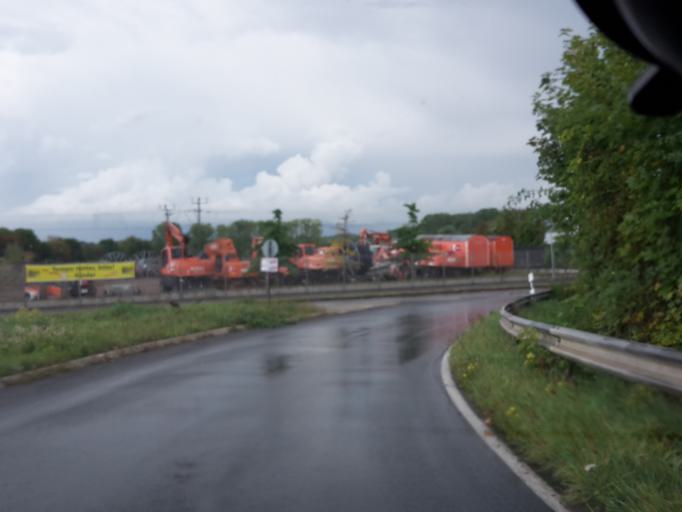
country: DE
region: Rheinland-Pfalz
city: Bodenheim
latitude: 49.9220
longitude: 8.3223
